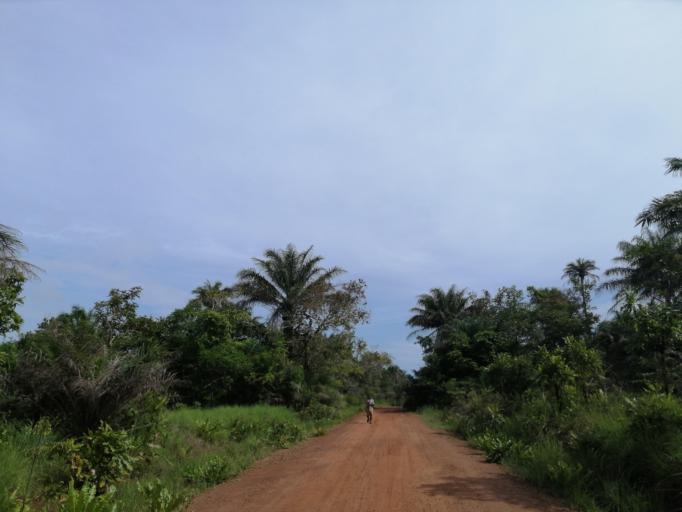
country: SL
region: Northern Province
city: Port Loko
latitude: 8.7807
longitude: -12.9212
